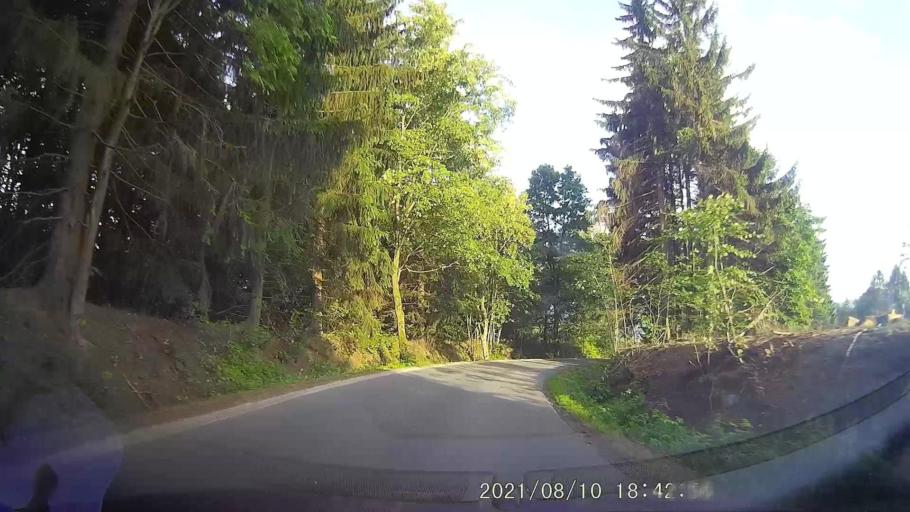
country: PL
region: Lower Silesian Voivodeship
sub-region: Powiat klodzki
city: Duszniki-Zdroj
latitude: 50.4474
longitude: 16.3494
